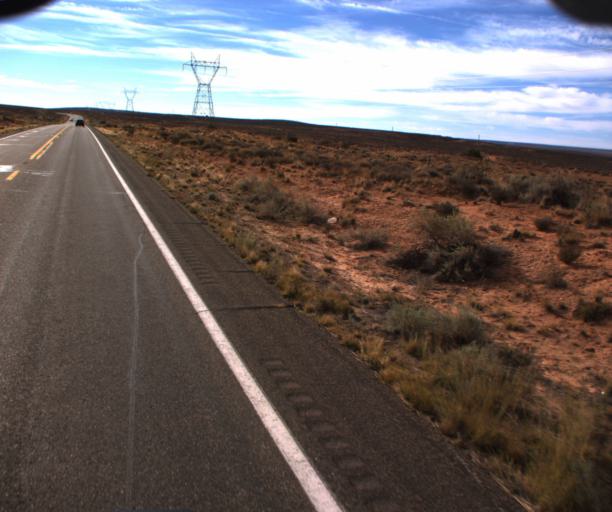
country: US
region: Arizona
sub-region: Coconino County
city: LeChee
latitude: 36.8482
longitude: -111.3317
